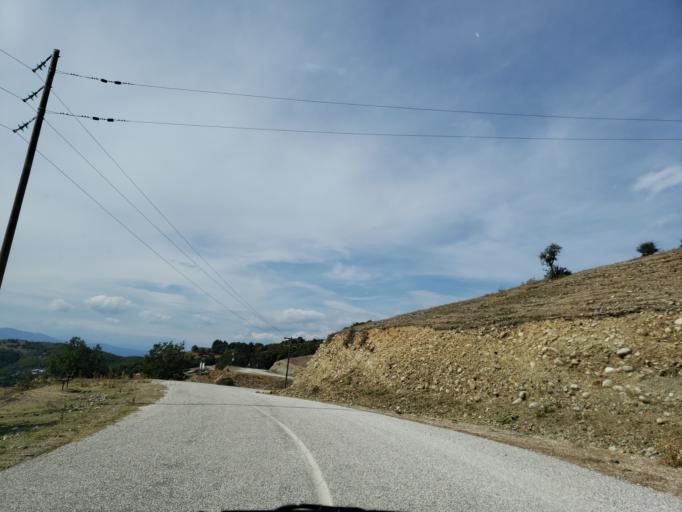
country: GR
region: Thessaly
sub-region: Trikala
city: Kastraki
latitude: 39.7683
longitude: 21.6656
